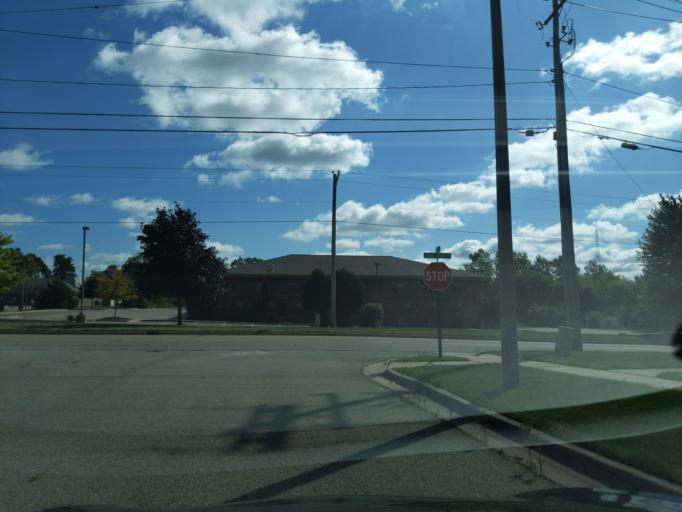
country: US
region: Michigan
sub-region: Ingham County
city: Holt
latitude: 42.6817
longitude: -84.5040
